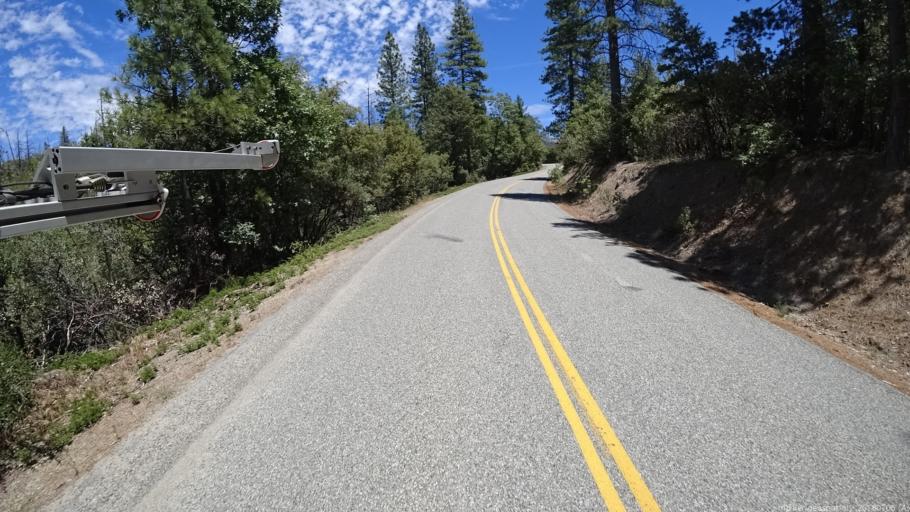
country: US
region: California
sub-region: Madera County
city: Oakhurst
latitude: 37.3420
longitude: -119.5541
